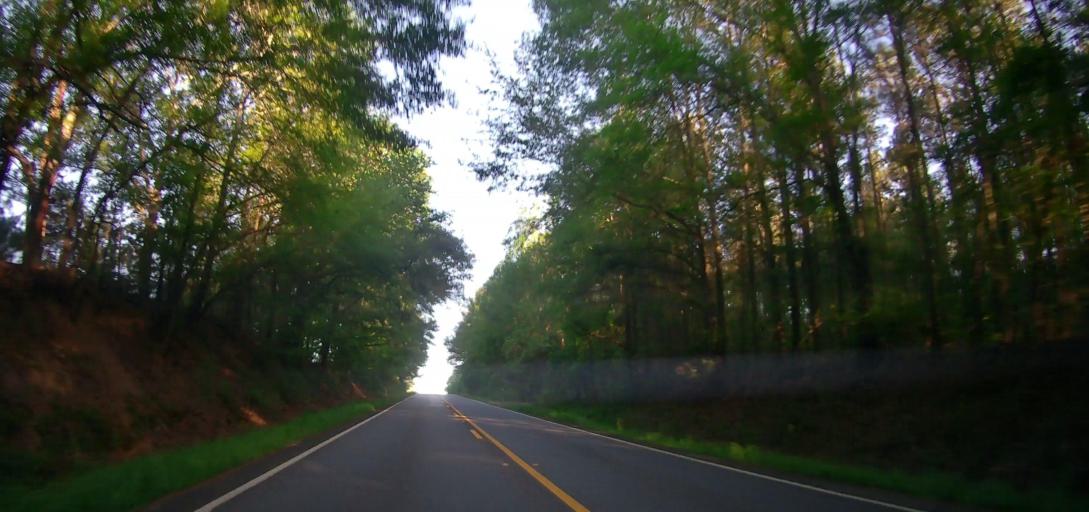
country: US
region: Georgia
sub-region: Marion County
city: Buena Vista
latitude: 32.3581
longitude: -84.3903
